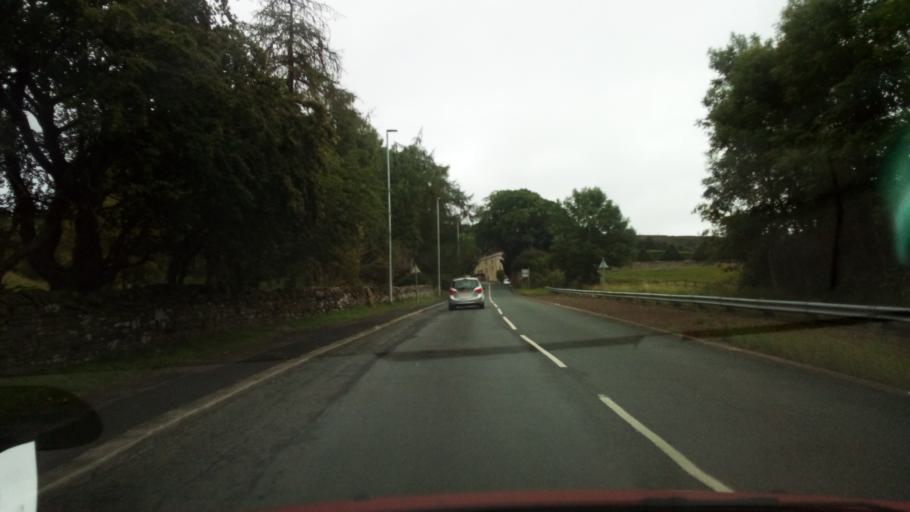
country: GB
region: England
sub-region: County Durham
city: Stanhope
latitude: 54.7555
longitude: -2.0156
